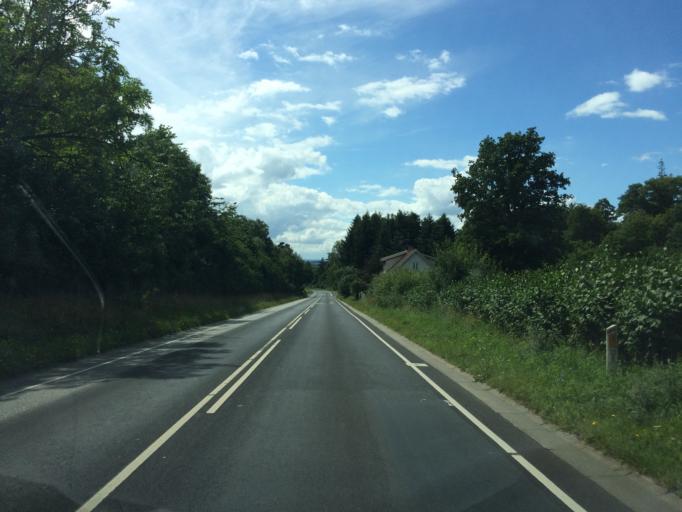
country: DK
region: South Denmark
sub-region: Faaborg-Midtfyn Kommune
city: Faaborg
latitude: 55.1245
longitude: 10.2526
